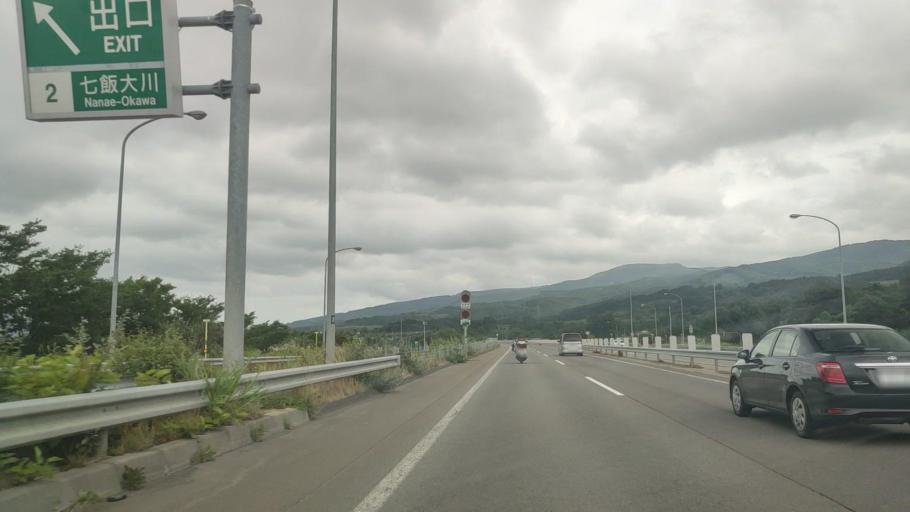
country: JP
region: Hokkaido
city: Nanae
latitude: 41.8664
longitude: 140.7301
